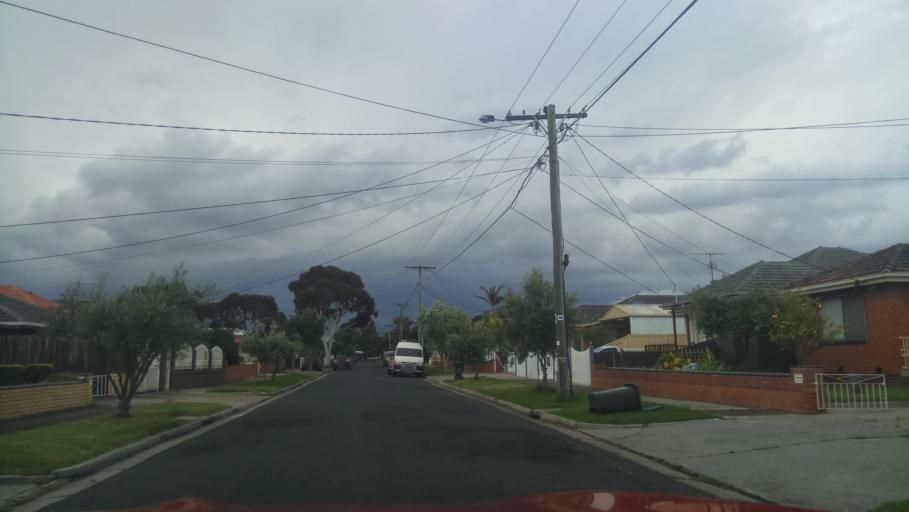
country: AU
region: Victoria
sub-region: Hobsons Bay
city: Altona North
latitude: -37.8413
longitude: 144.8486
